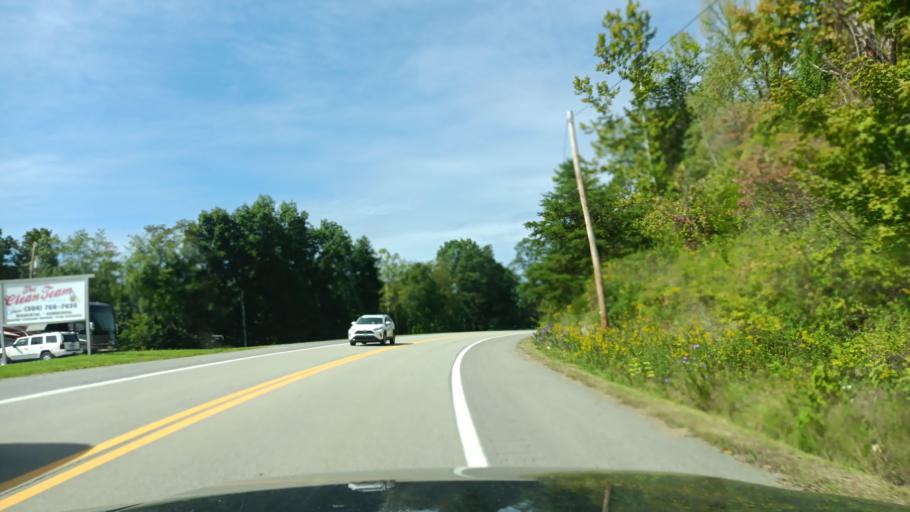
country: US
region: West Virginia
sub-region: Harrison County
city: Bridgeport
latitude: 39.2855
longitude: -80.2362
